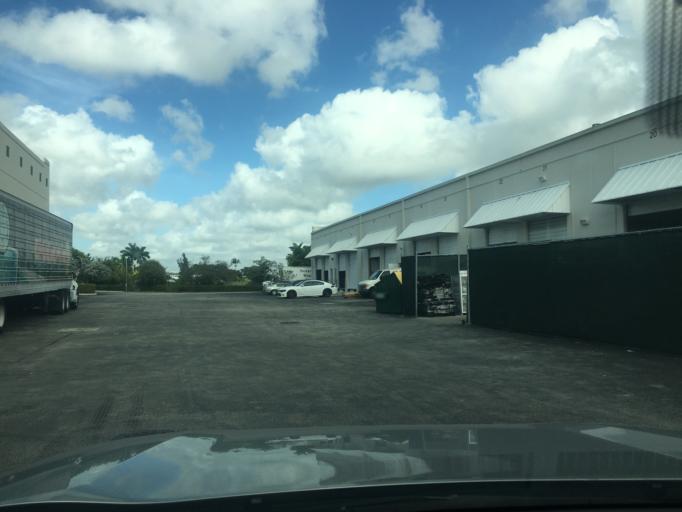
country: US
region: Florida
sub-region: Broward County
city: Broadview Park
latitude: 26.0763
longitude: -80.1827
